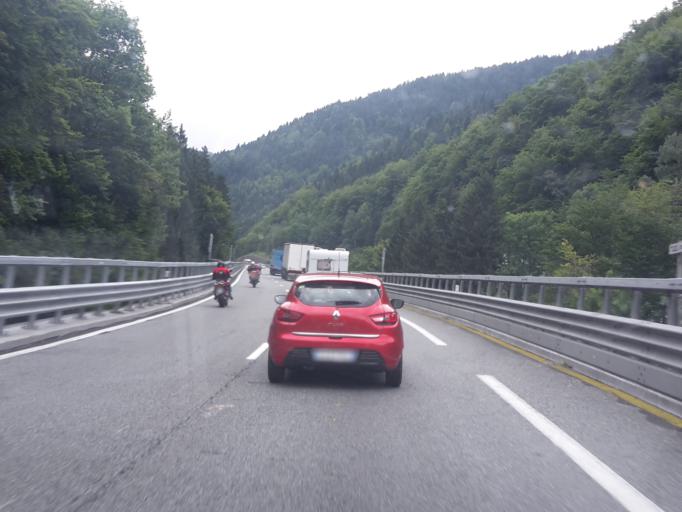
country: FR
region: Rhone-Alpes
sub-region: Departement de la Haute-Savoie
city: Saint-Gervais-les-Bains
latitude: 45.9310
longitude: 6.7393
